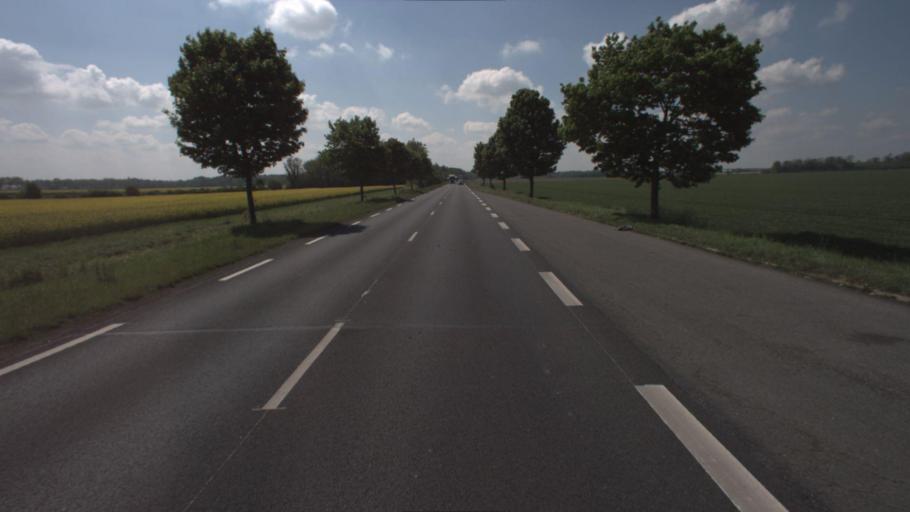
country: FR
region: Ile-de-France
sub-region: Departement de Seine-et-Marne
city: La Houssaye-en-Brie
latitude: 48.7465
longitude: 2.8577
